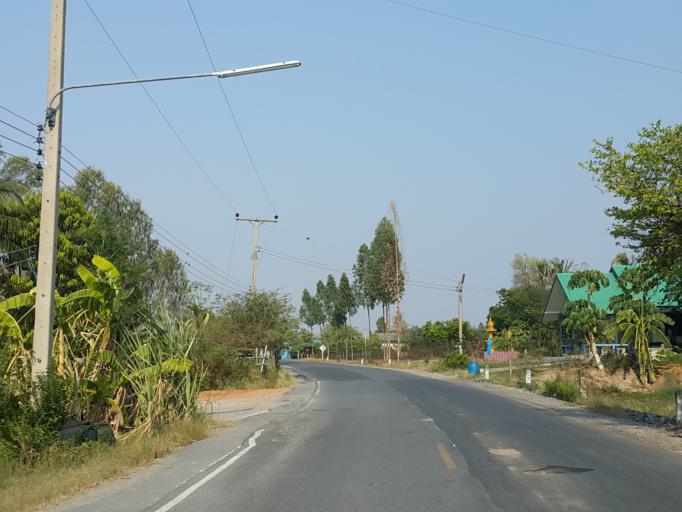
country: TH
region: Suphan Buri
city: Sam Chuk
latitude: 14.7451
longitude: 100.0401
